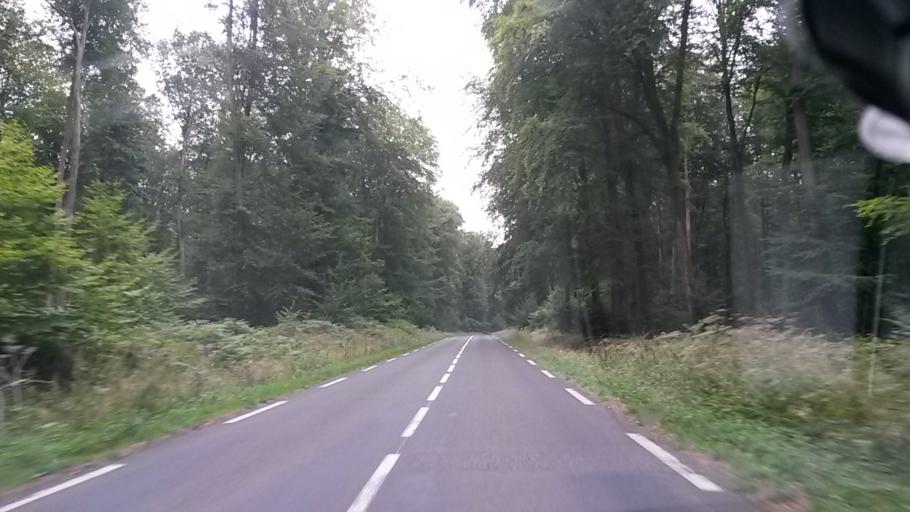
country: FR
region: Haute-Normandie
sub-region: Departement de l'Eure
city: Charleval
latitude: 49.3816
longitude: 1.4688
